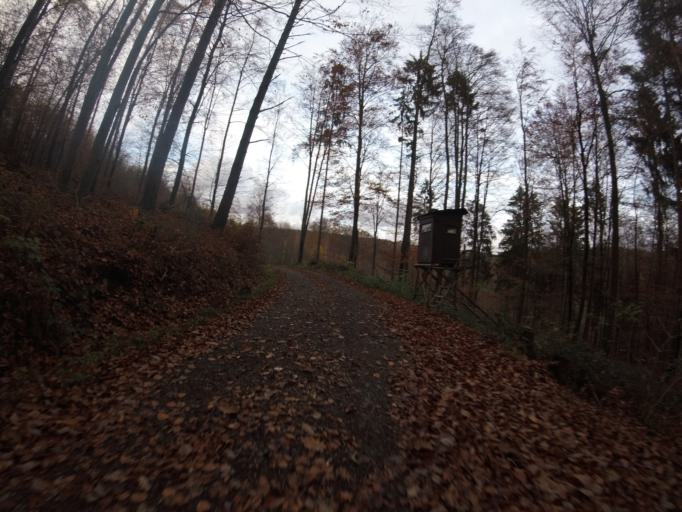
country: DE
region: Baden-Wuerttemberg
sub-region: Regierungsbezirk Stuttgart
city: Aspach
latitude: 49.0018
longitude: 9.3923
